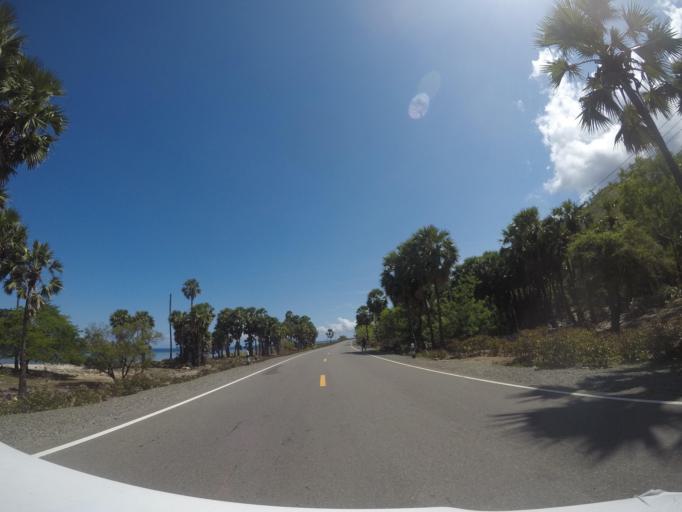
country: ID
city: Metinaro
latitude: -8.4878
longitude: 125.8340
